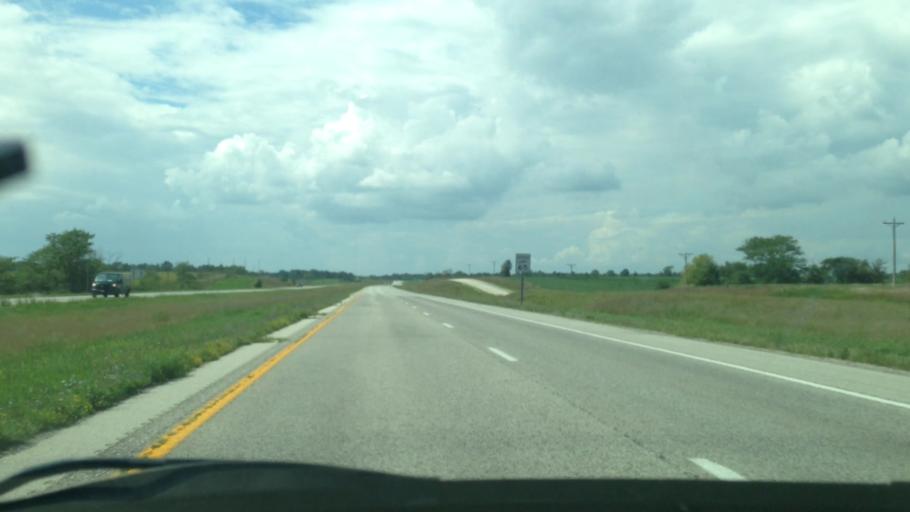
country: US
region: Missouri
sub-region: Pike County
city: Bowling Green
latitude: 39.2508
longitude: -91.0368
